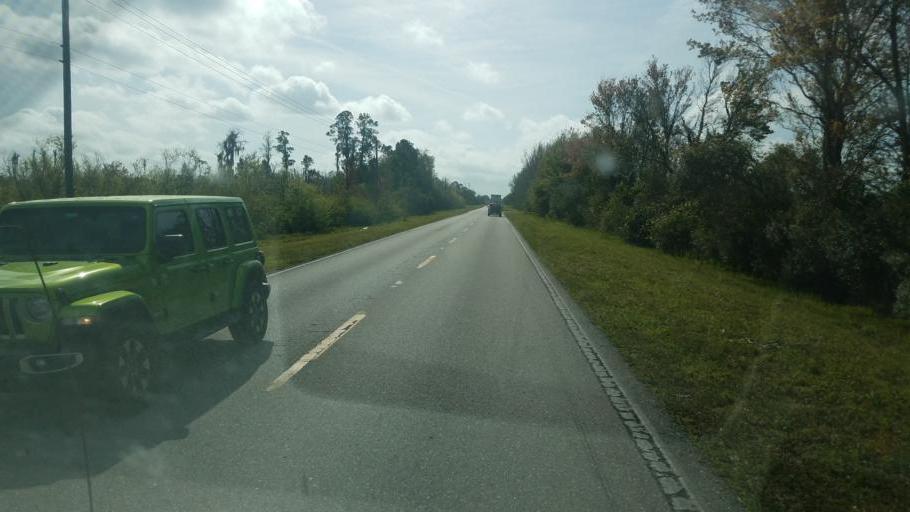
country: US
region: Florida
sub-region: Polk County
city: Polk City
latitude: 28.1969
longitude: -81.7515
